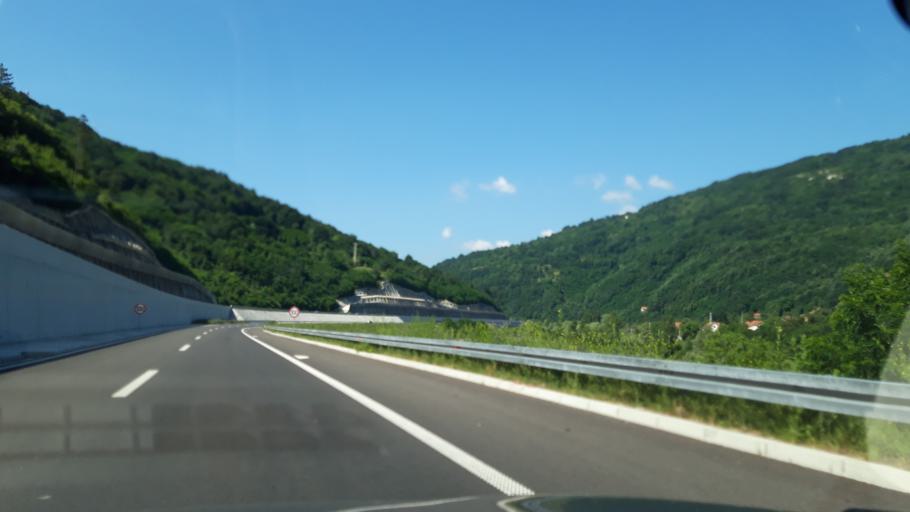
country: RS
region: Central Serbia
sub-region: Pcinjski Okrug
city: Vladicin Han
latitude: 42.7718
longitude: 22.0858
